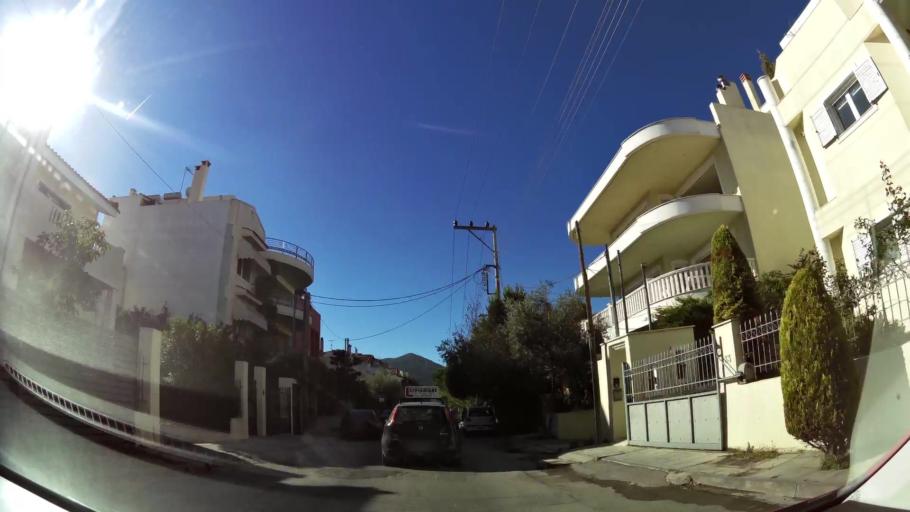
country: GR
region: Attica
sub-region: Nomarchia Athinas
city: Agia Paraskevi
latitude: 38.0186
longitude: 23.8425
